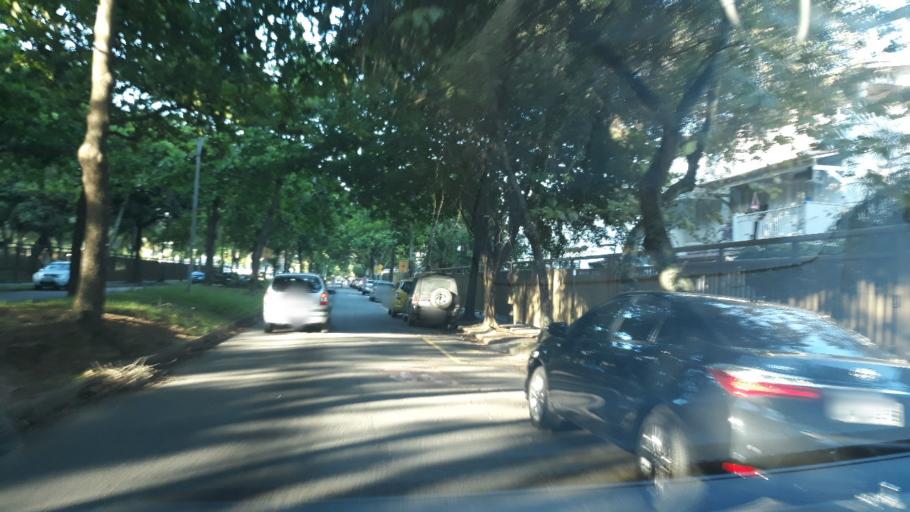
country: BR
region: Rio de Janeiro
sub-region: Rio De Janeiro
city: Rio de Janeiro
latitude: -23.0051
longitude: -43.3388
